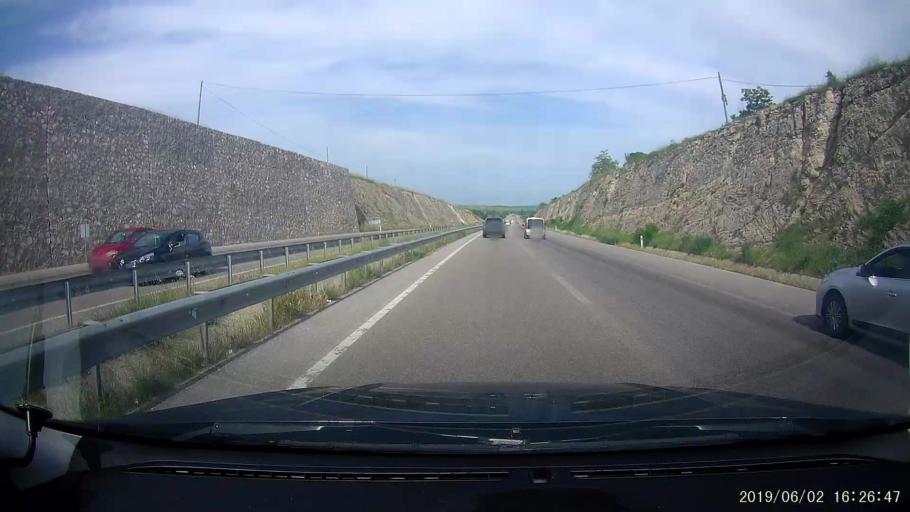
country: TR
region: Samsun
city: Ladik
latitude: 41.0015
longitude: 35.8113
